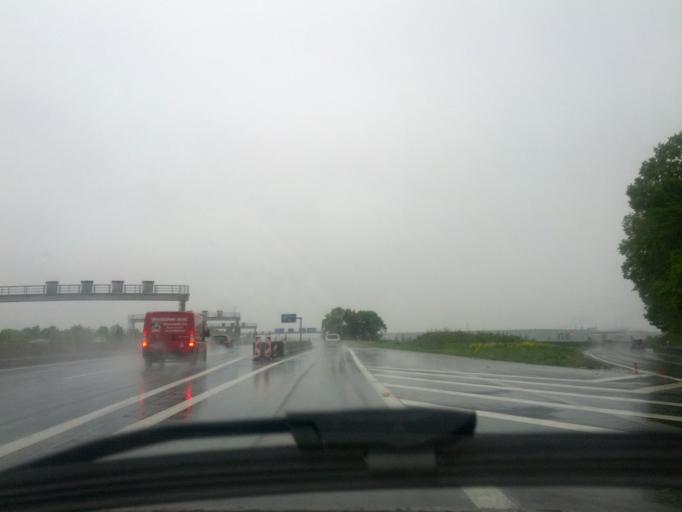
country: DE
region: North Rhine-Westphalia
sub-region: Regierungsbezirk Koln
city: Frechen
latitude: 50.9284
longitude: 6.8468
